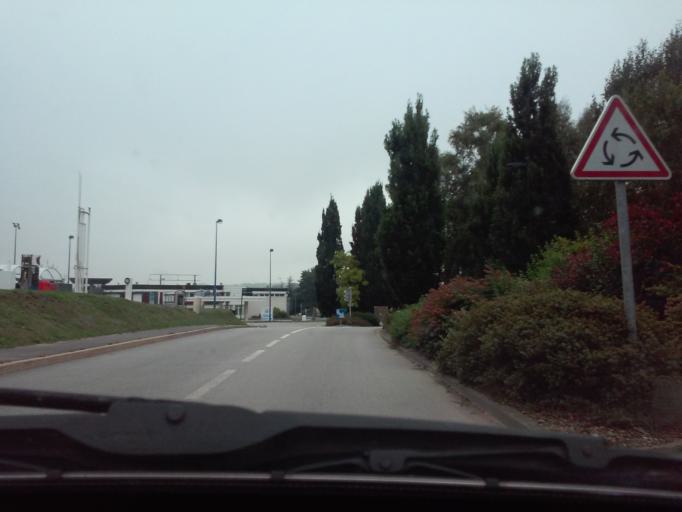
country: FR
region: Brittany
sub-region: Departement du Morbihan
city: Josselin
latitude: 47.9617
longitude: -2.5466
